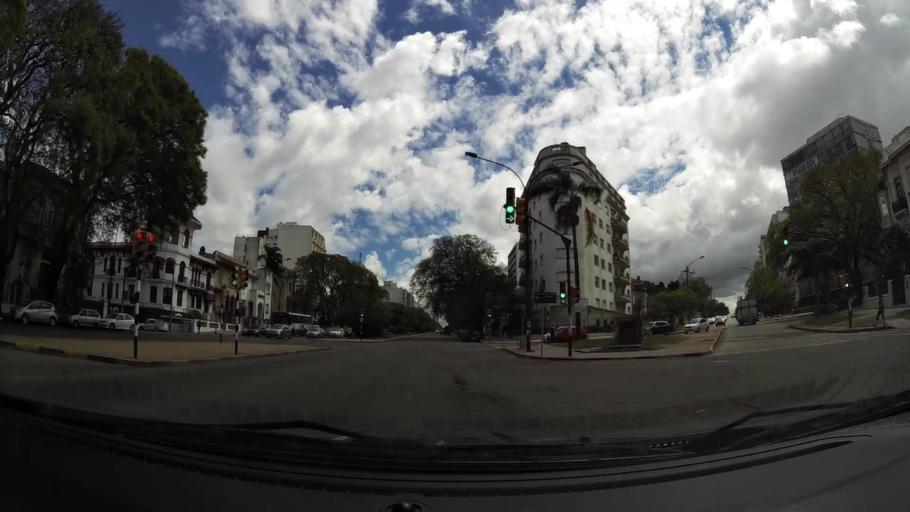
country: UY
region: Montevideo
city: Montevideo
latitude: -34.9059
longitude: -56.1636
